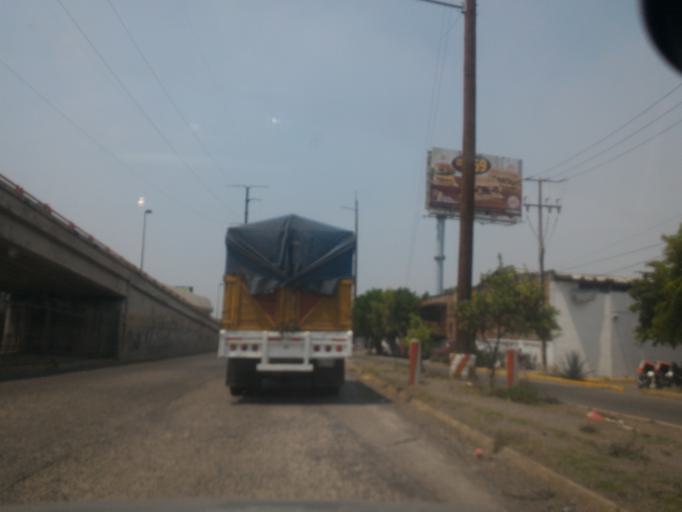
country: MX
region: Jalisco
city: Guadalajara
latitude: 20.6263
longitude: -103.3851
